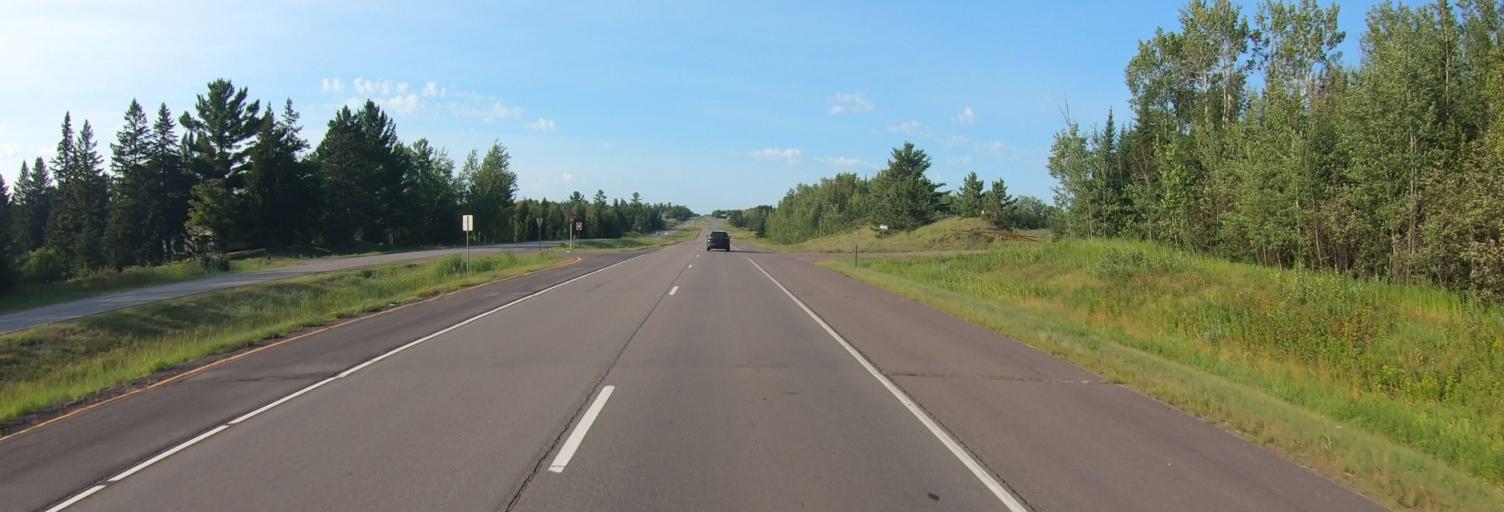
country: US
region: Minnesota
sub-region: Carlton County
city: Cloquet
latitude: 47.0189
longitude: -92.4708
